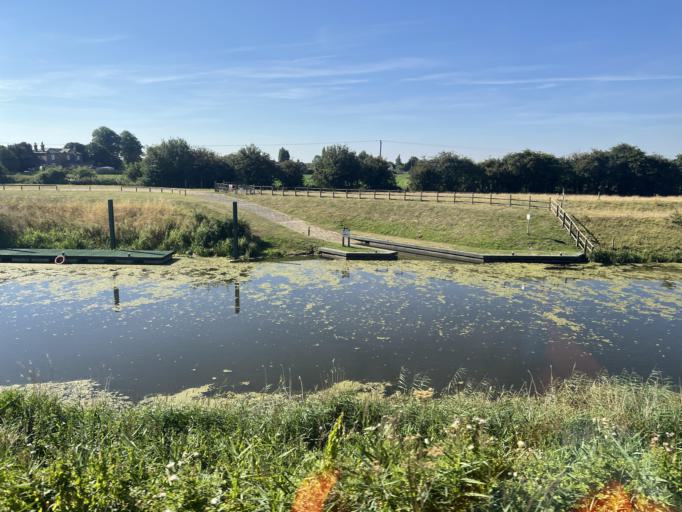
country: GB
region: England
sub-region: Lincolnshire
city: Kirton
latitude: 52.9756
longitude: -0.1141
